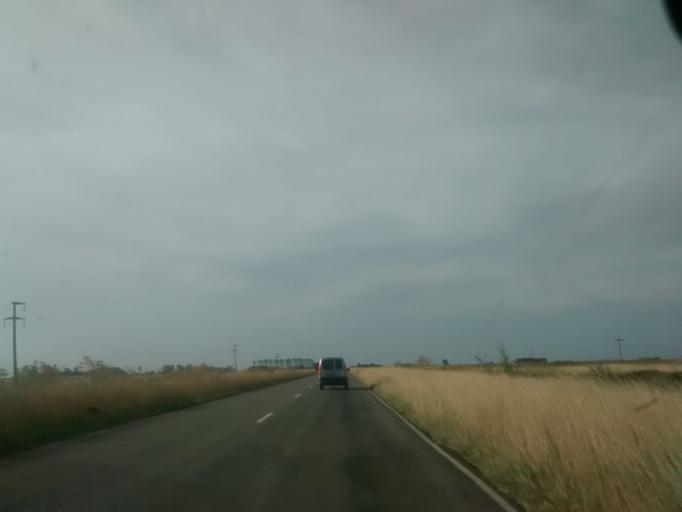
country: AR
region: Buenos Aires
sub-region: Partido de Ayacucho
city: Ayacucho
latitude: -36.9071
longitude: -58.5274
